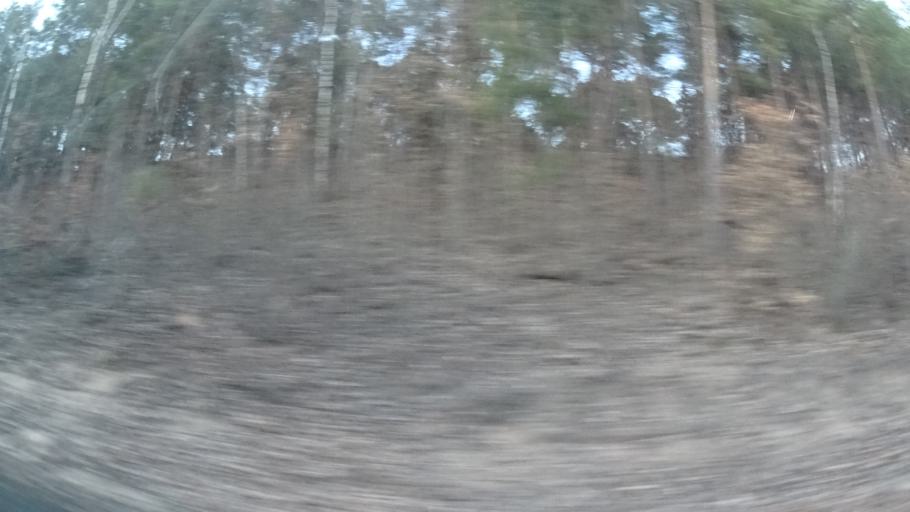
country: DE
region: Bavaria
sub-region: Regierungsbezirk Unterfranken
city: Alzenau in Unterfranken
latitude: 50.0989
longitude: 9.0595
